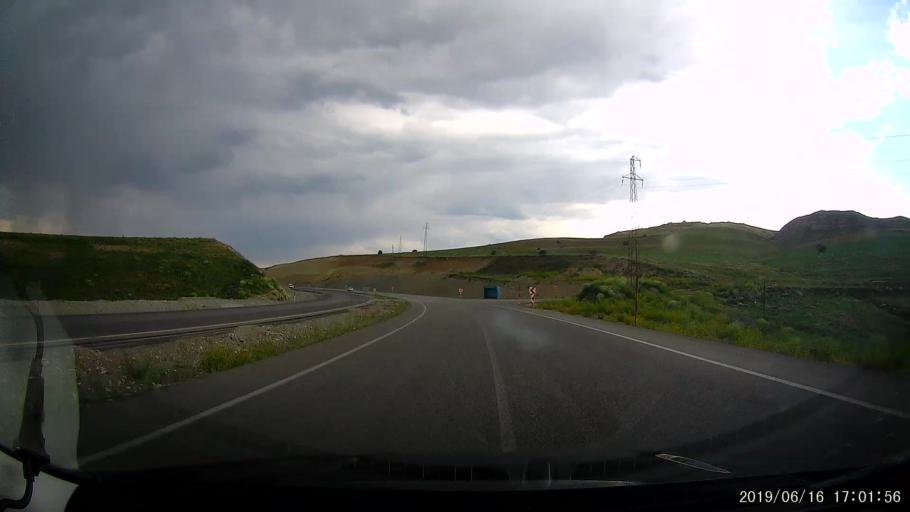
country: TR
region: Erzurum
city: Askale
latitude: 39.9438
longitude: 40.7644
